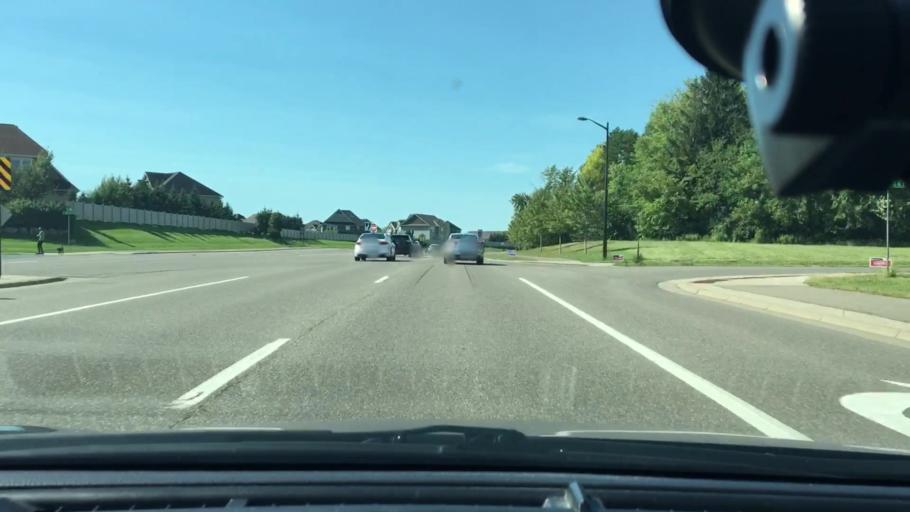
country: US
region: Minnesota
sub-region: Hennepin County
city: Maple Grove
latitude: 45.0838
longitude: -93.4976
